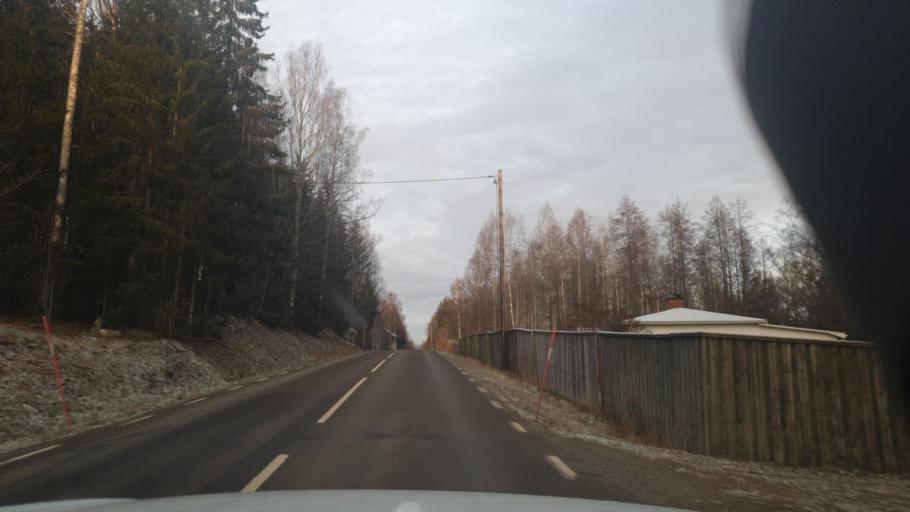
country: SE
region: Vaermland
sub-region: Arvika Kommun
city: Arvika
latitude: 59.6284
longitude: 12.4968
